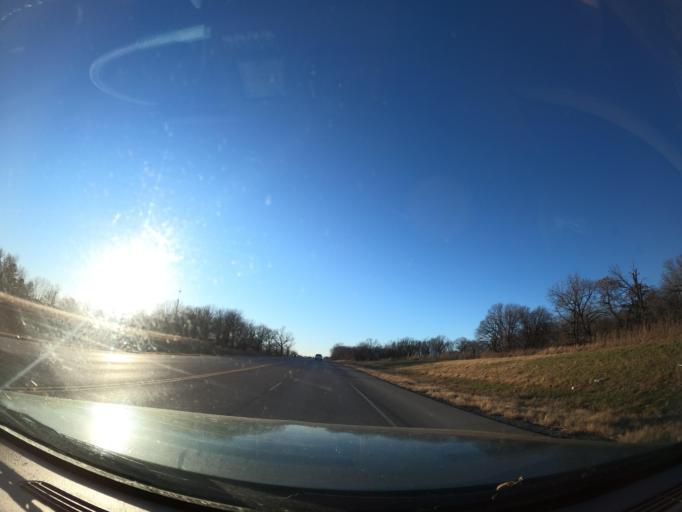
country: US
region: Oklahoma
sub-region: Pittsburg County
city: Hartshorne
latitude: 34.8940
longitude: -95.6312
